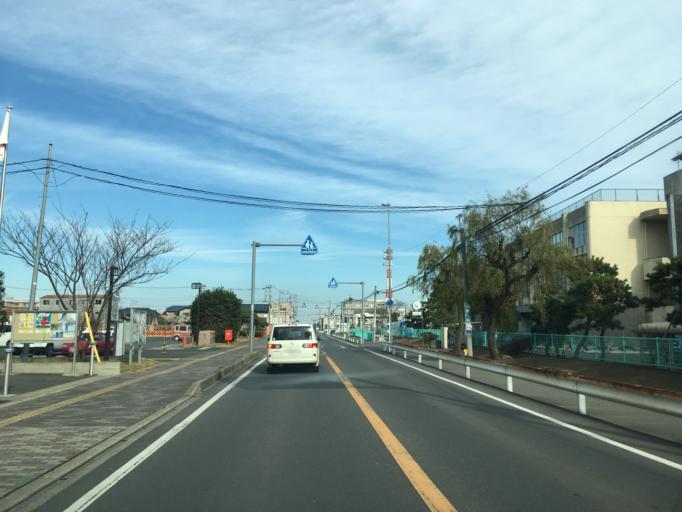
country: JP
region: Chiba
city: Katori-shi
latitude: 35.8969
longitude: 140.4995
